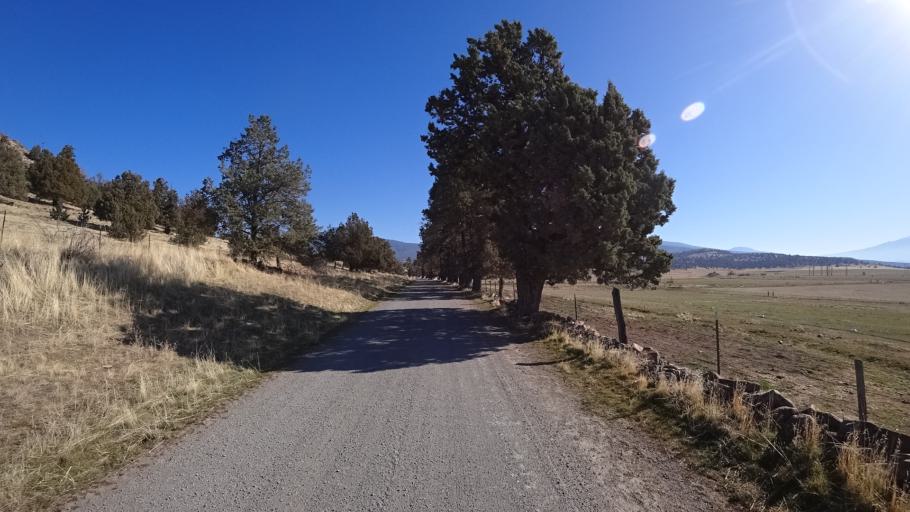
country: US
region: California
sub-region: Siskiyou County
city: Montague
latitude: 41.6877
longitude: -122.3671
